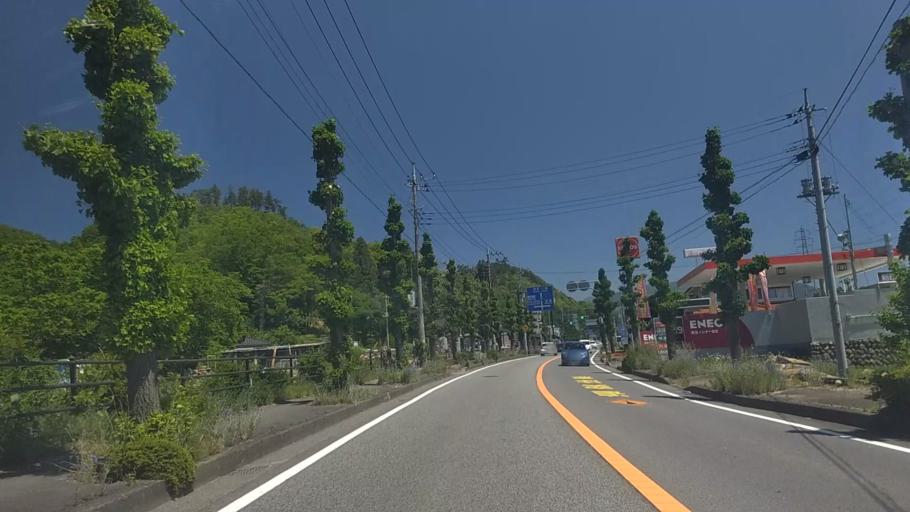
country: JP
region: Yamanashi
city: Nirasaki
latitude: 35.7904
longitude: 138.4187
